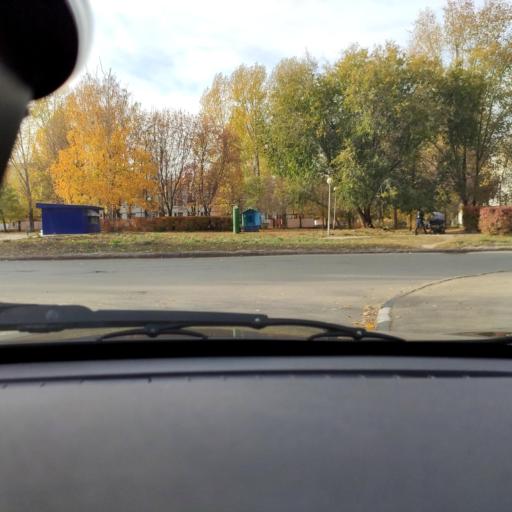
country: RU
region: Samara
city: Tol'yatti
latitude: 53.5305
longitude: 49.3046
